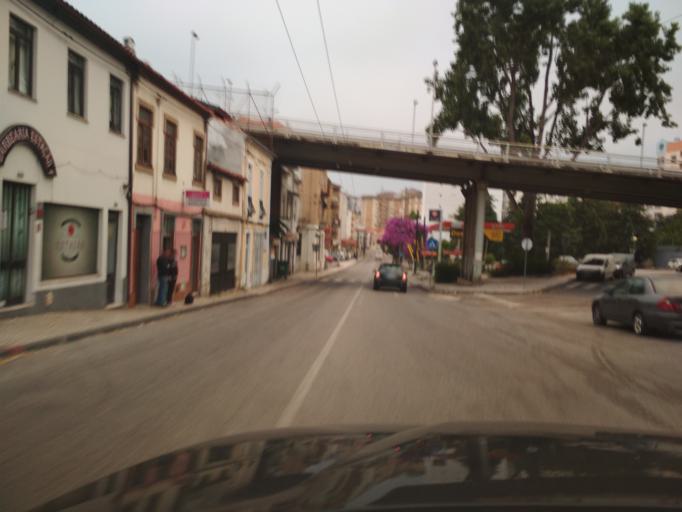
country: PT
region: Coimbra
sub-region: Coimbra
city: Coimbra
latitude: 40.2010
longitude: -8.4079
